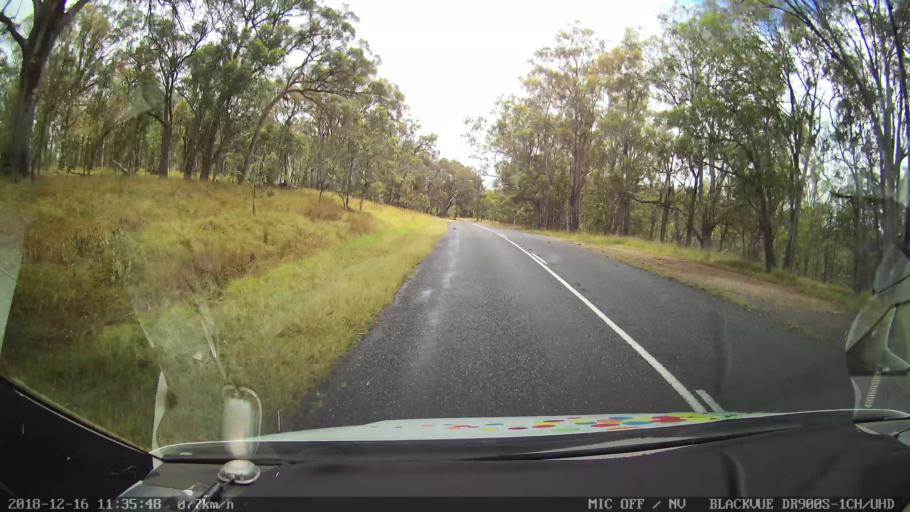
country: AU
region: New South Wales
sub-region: Tenterfield Municipality
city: Carrolls Creek
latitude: -28.9865
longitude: 152.1654
